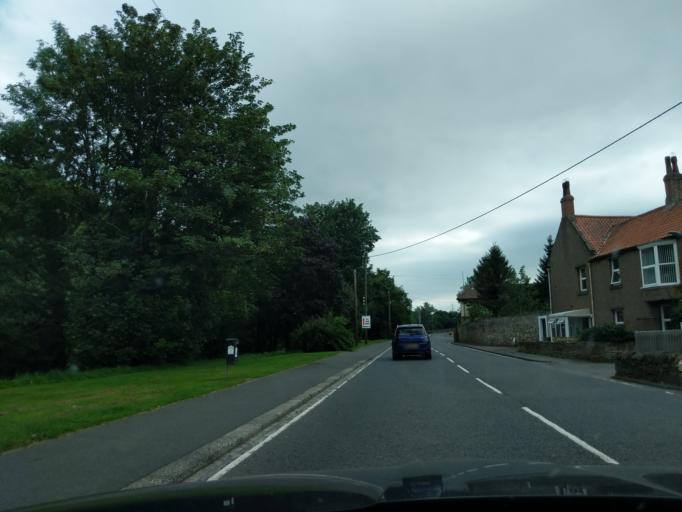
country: GB
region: England
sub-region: Northumberland
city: Wooler
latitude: 55.5472
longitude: -2.0113
